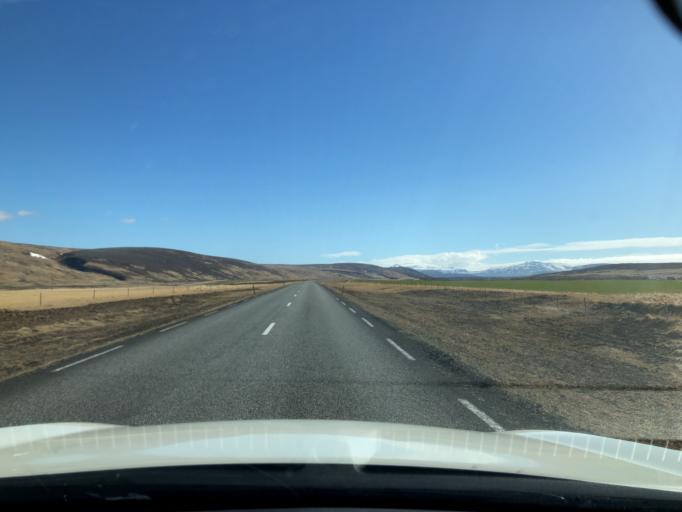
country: IS
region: South
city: Hveragerdi
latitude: 64.6997
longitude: -21.2248
